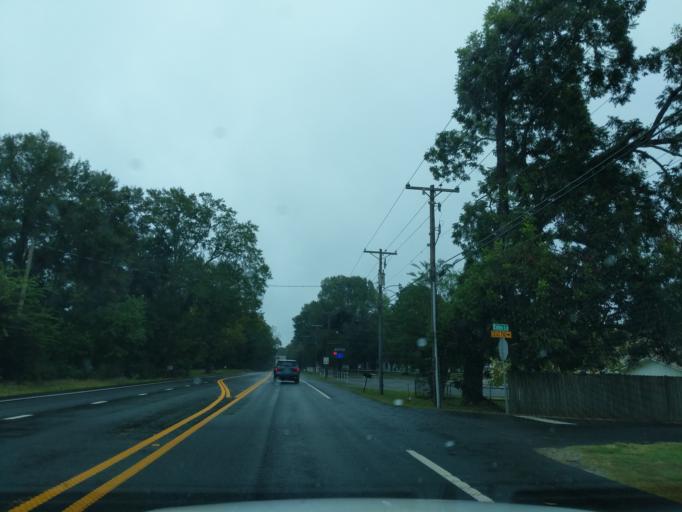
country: US
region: Louisiana
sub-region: Caddo Parish
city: Greenwood
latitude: 32.3735
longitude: -94.0415
